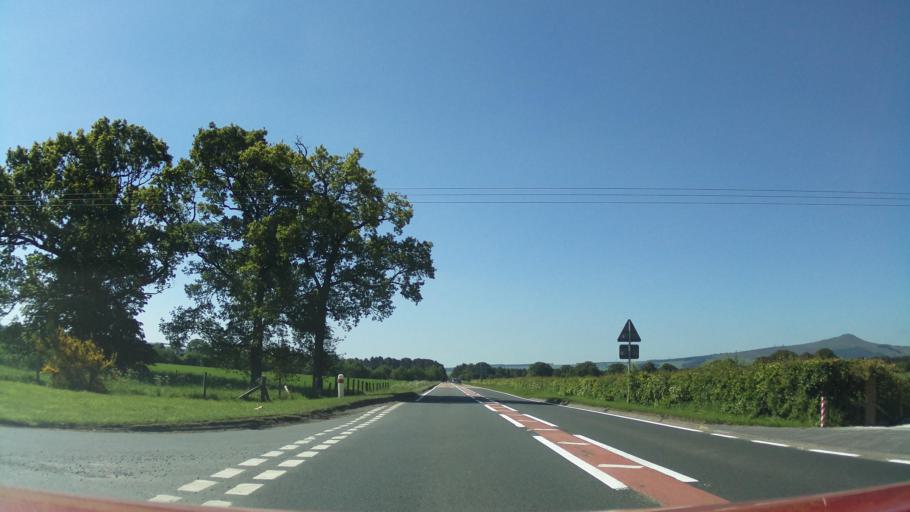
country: GB
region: Scotland
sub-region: Fife
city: Ladybank
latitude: 56.2842
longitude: -3.1318
